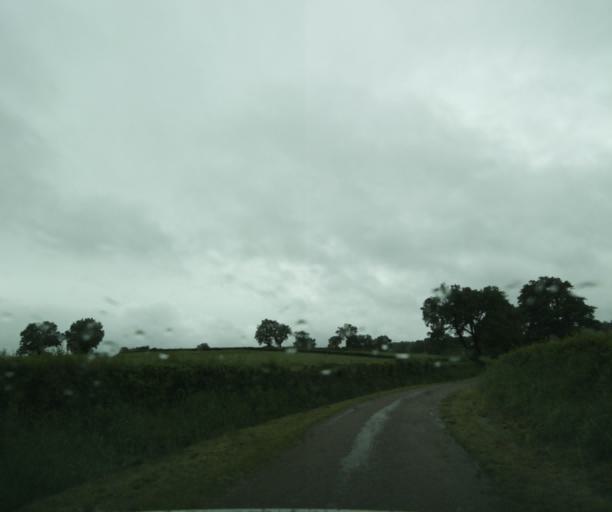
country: FR
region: Bourgogne
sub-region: Departement de Saone-et-Loire
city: Charolles
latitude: 46.4699
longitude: 4.2943
